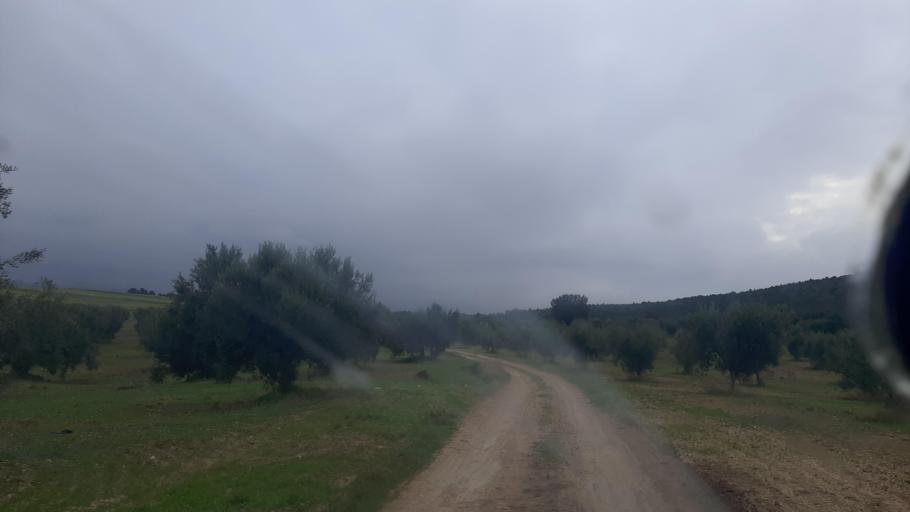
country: TN
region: Tunis
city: La Sebala du Mornag
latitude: 36.5800
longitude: 10.2898
